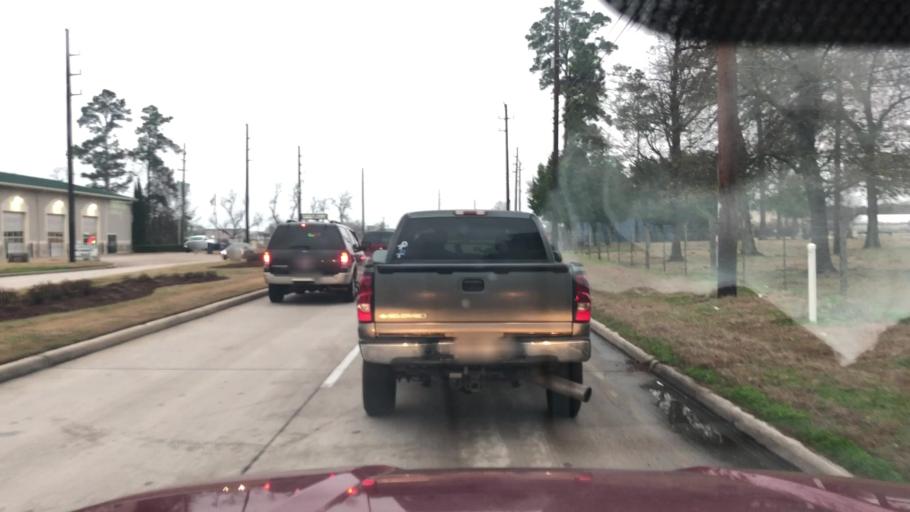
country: US
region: Texas
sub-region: Harris County
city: Tomball
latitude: 30.0393
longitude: -95.5371
